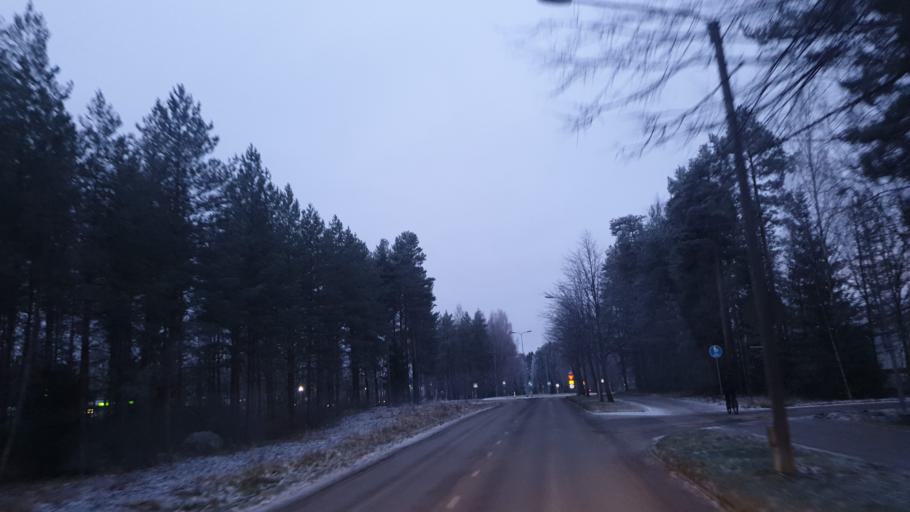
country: FI
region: Southern Ostrobothnia
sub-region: Seinaejoki
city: Seinaejoki
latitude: 62.7728
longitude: 22.8769
